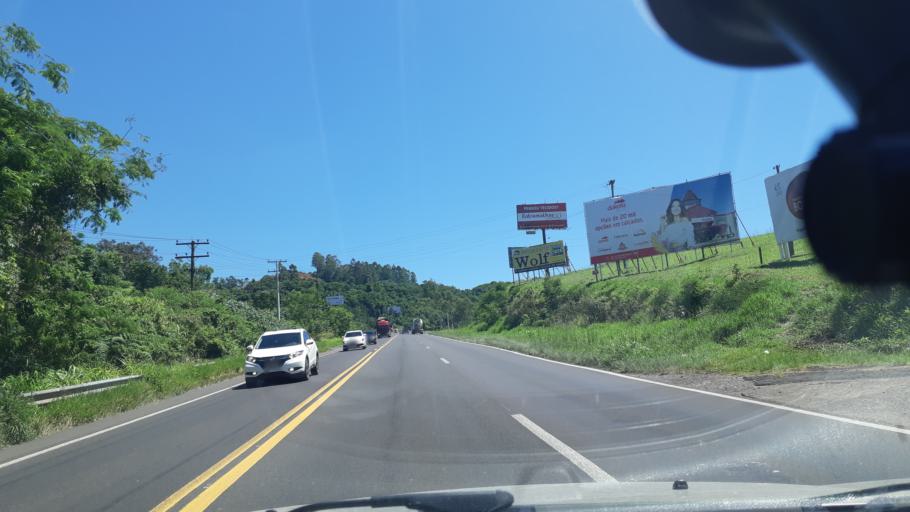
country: BR
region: Rio Grande do Sul
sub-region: Estancia Velha
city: Estancia Velha
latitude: -29.6359
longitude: -51.1423
